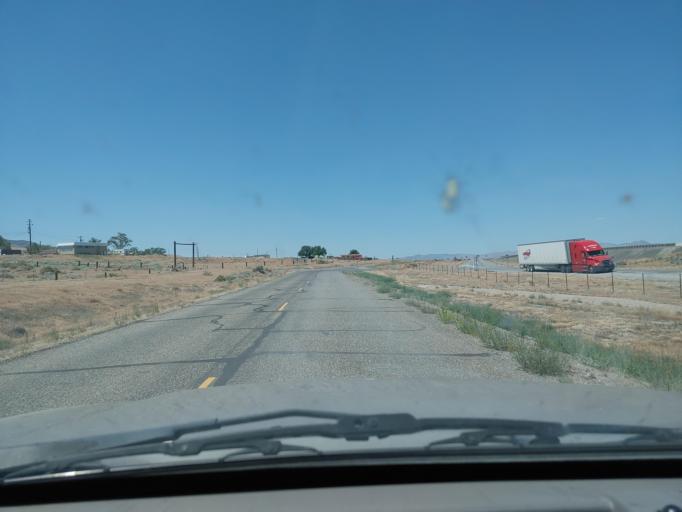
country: US
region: Nevada
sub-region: Humboldt County
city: Winnemucca
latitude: 40.6568
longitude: -118.1444
